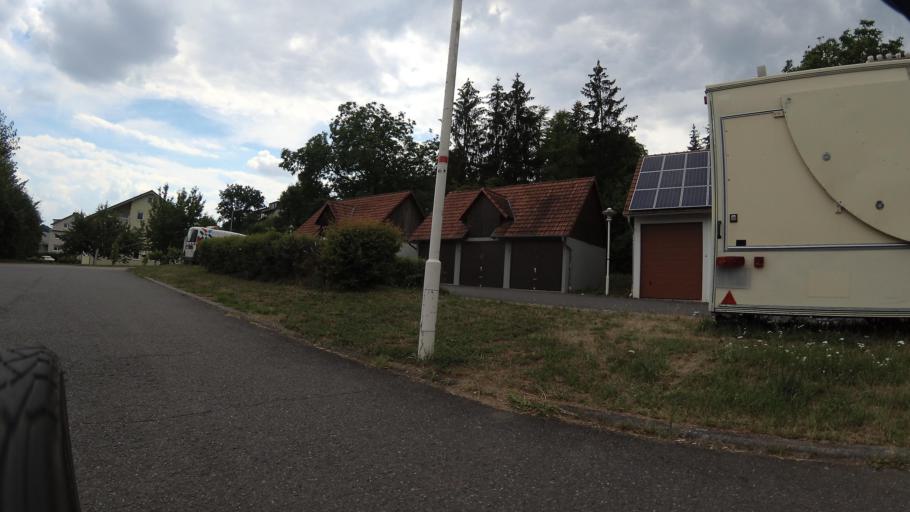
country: DE
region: Baden-Wuerttemberg
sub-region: Regierungsbezirk Stuttgart
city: Neudenau
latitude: 49.2802
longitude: 9.2538
